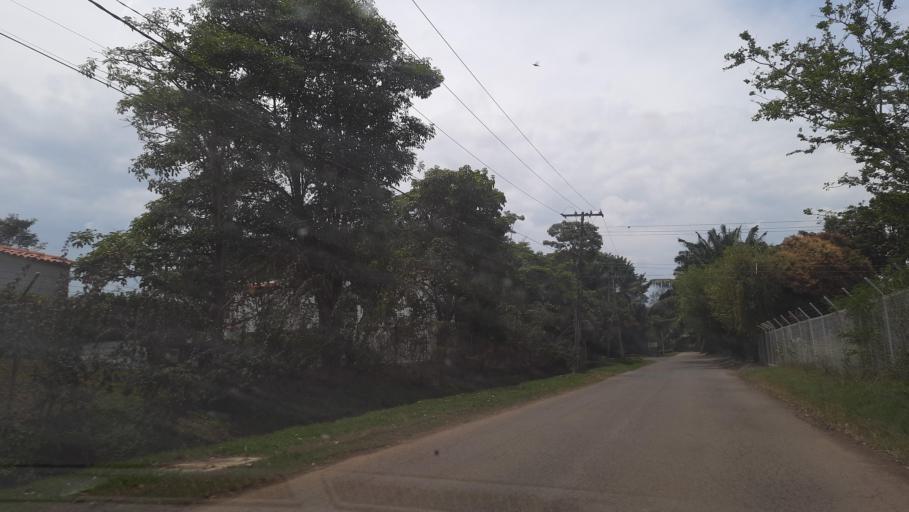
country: CO
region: Valle del Cauca
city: Jamundi
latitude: 3.2679
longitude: -76.5120
